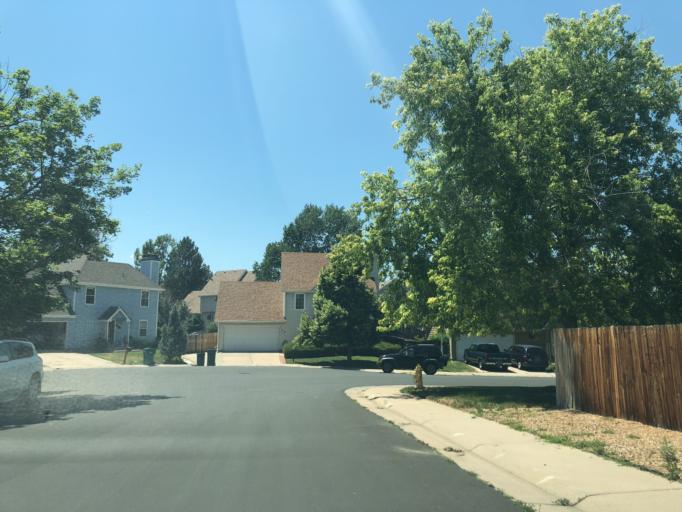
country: US
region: Colorado
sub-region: Arapahoe County
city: Dove Valley
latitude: 39.6246
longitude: -104.7760
